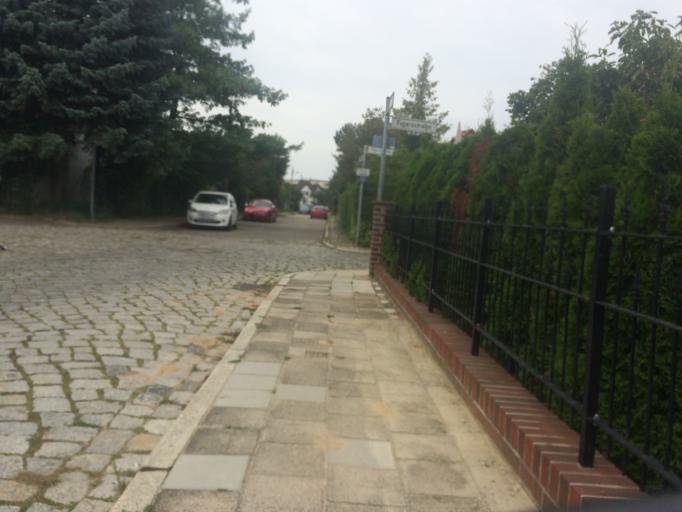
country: DE
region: Berlin
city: Heinersdorf
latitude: 52.5670
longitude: 13.4315
